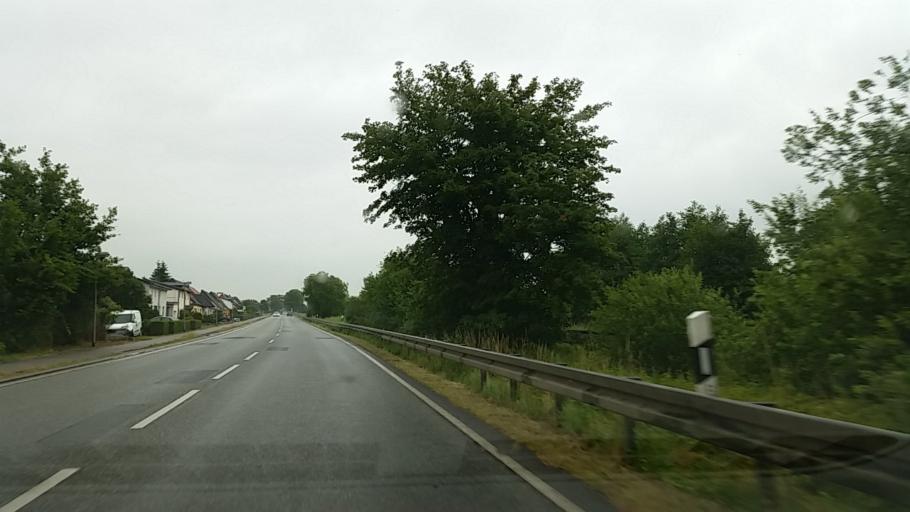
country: DE
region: Mecklenburg-Vorpommern
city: Biendorf
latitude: 54.0458
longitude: 11.7136
